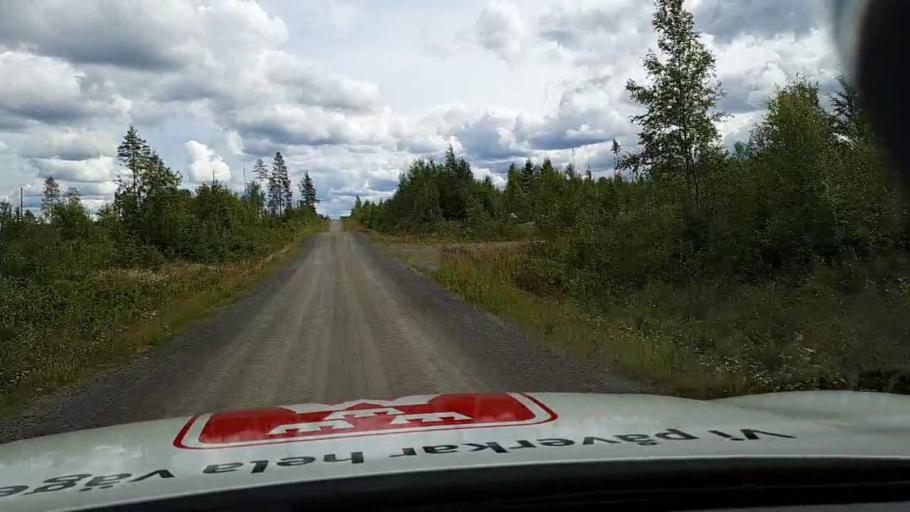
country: SE
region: Jaemtland
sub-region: OEstersunds Kommun
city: Lit
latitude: 63.2959
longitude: 15.3331
